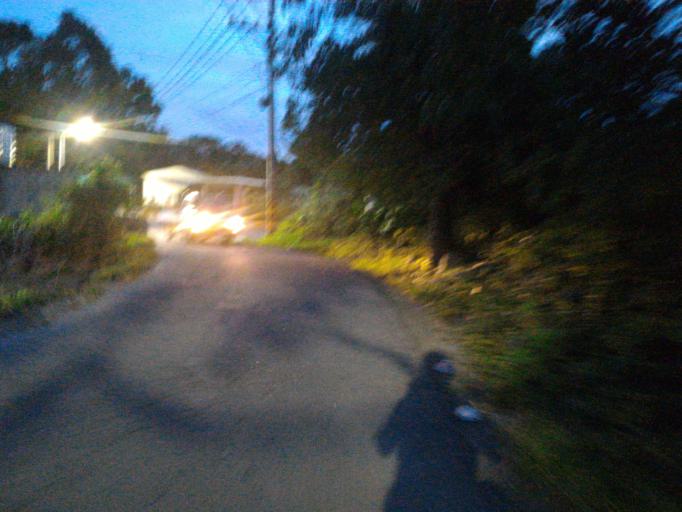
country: TW
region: Taipei
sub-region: Taipei
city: Banqiao
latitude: 24.9623
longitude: 121.4044
